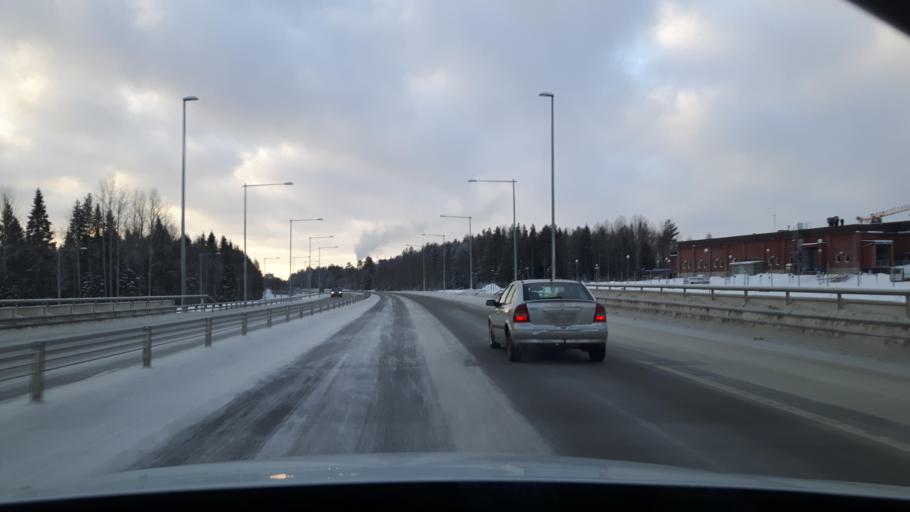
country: SE
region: Vaesterbotten
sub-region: Umea Kommun
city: Ersmark
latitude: 63.8325
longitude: 20.3327
